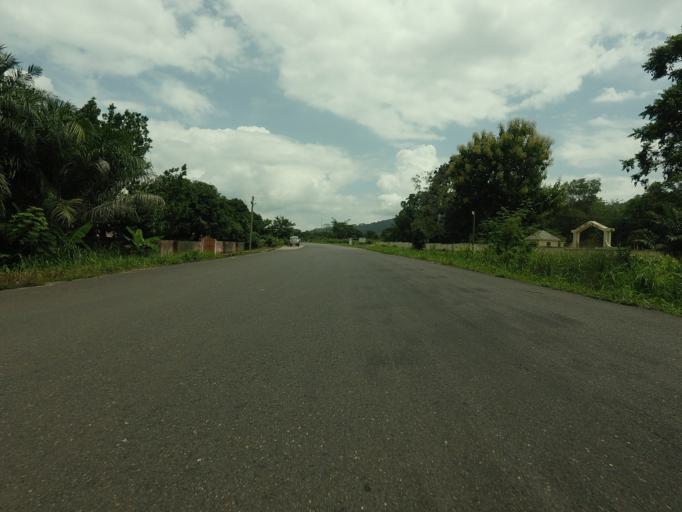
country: GH
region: Volta
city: Ho
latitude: 6.5385
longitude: 0.2343
